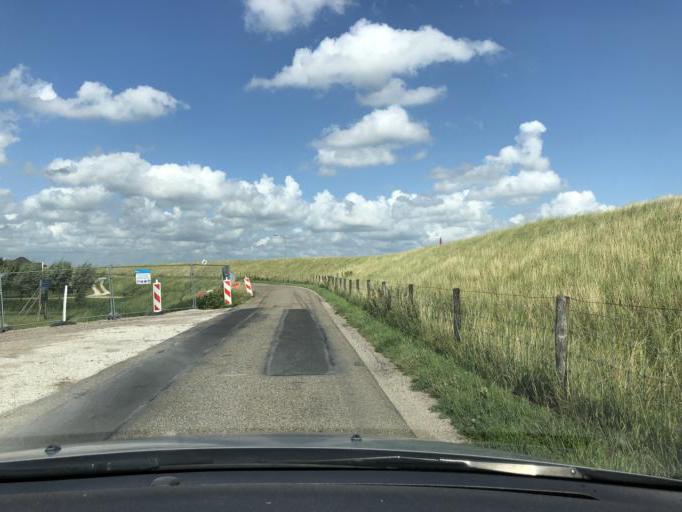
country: NL
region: North Holland
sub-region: Gemeente Hoorn
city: Hoorn
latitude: 52.6107
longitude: 5.0190
